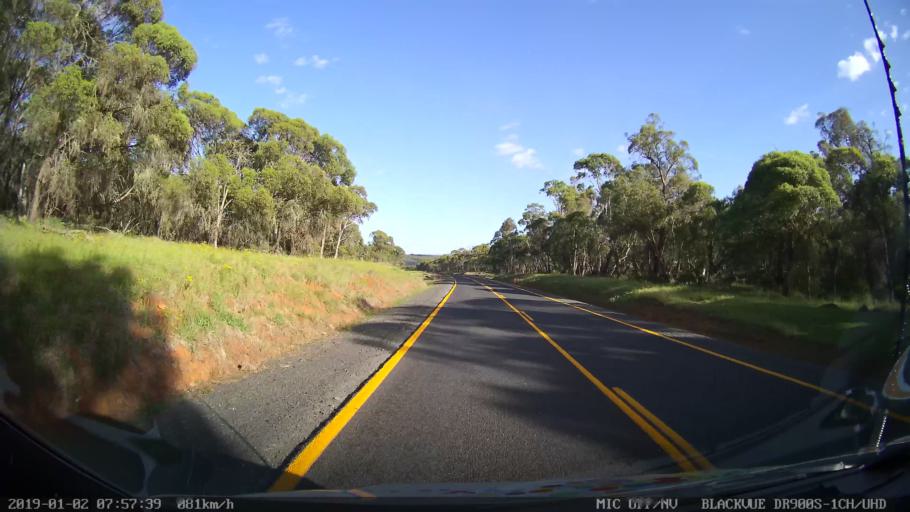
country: AU
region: New South Wales
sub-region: Tumut Shire
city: Tumut
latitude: -35.6613
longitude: 148.4726
